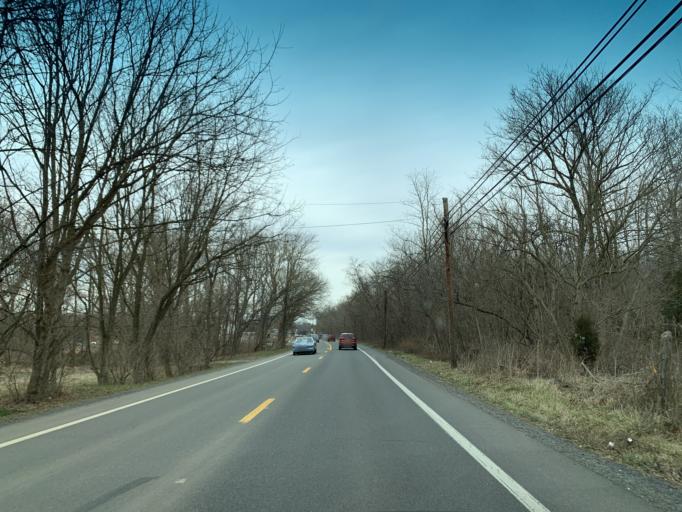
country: US
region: West Virginia
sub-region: Berkeley County
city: Martinsburg
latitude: 39.5112
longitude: -77.9322
